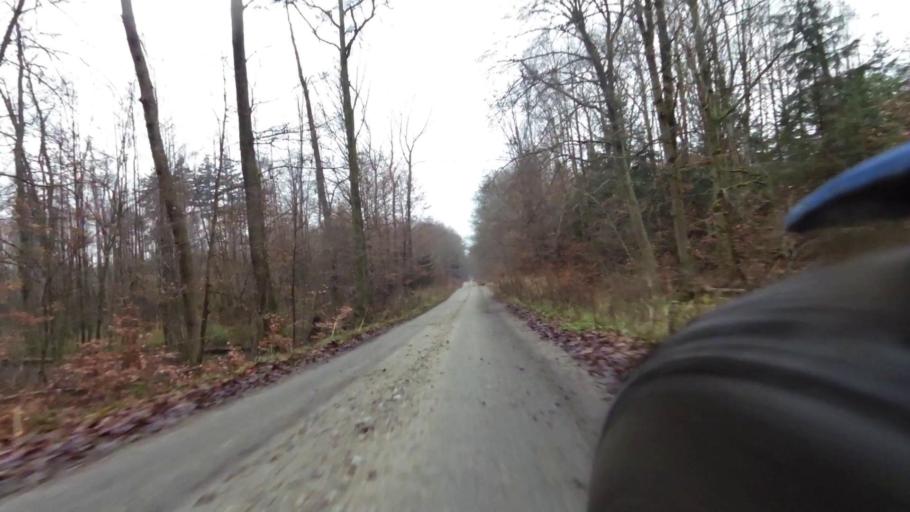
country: PL
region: West Pomeranian Voivodeship
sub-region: Powiat szczecinecki
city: Szczecinek
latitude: 53.6731
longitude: 16.6507
